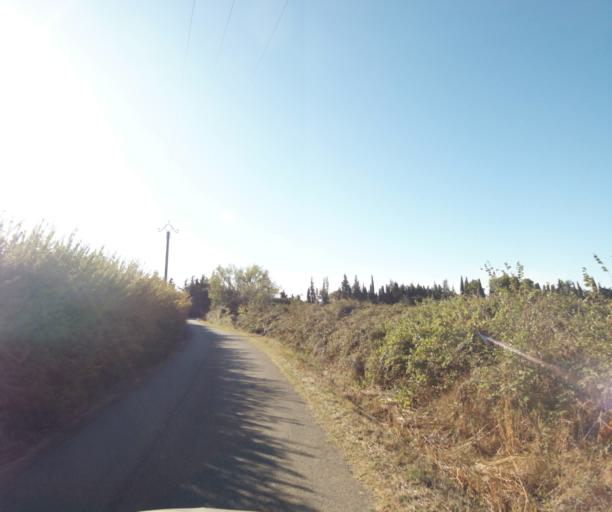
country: FR
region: Languedoc-Roussillon
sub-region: Departement du Gard
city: Bouillargues
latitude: 43.7890
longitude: 4.4594
